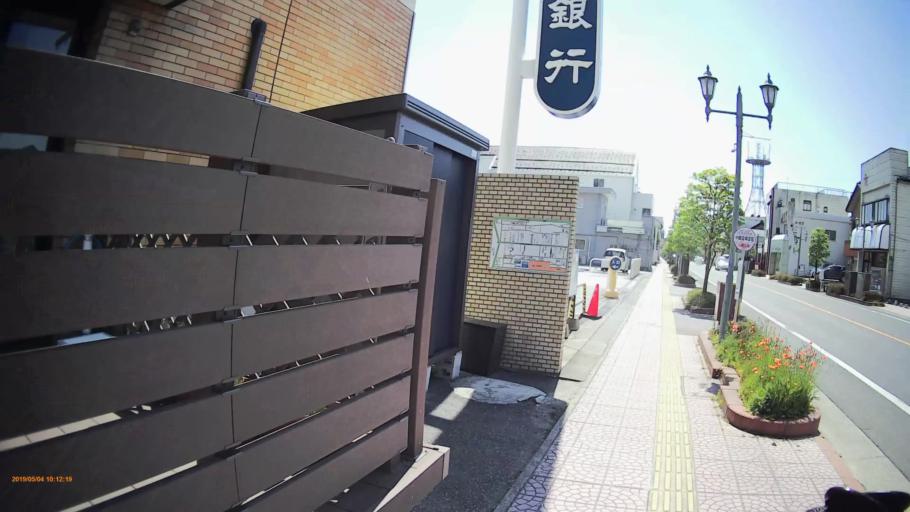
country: JP
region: Yamanashi
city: Nirasaki
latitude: 35.7066
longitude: 138.4512
